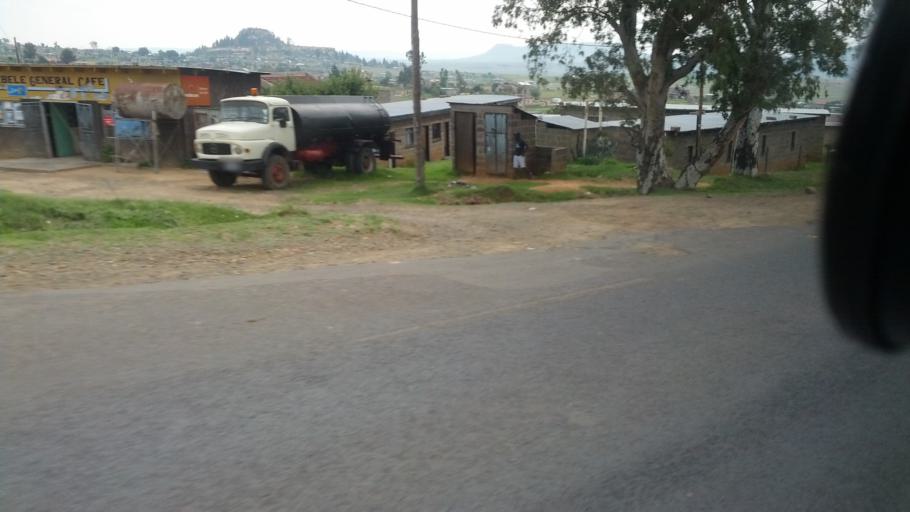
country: LS
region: Berea
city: Teyateyaneng
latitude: -29.1330
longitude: 27.7582
